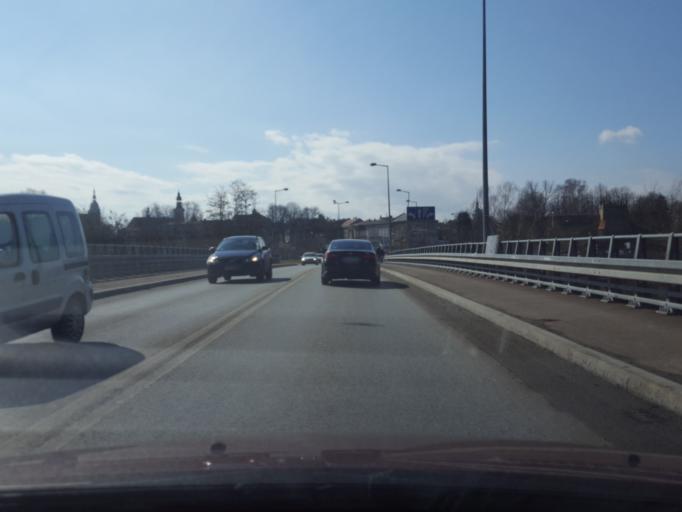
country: PL
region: Lesser Poland Voivodeship
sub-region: Powiat nowosadecki
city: Nowy Sacz
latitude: 49.6307
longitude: 20.6914
